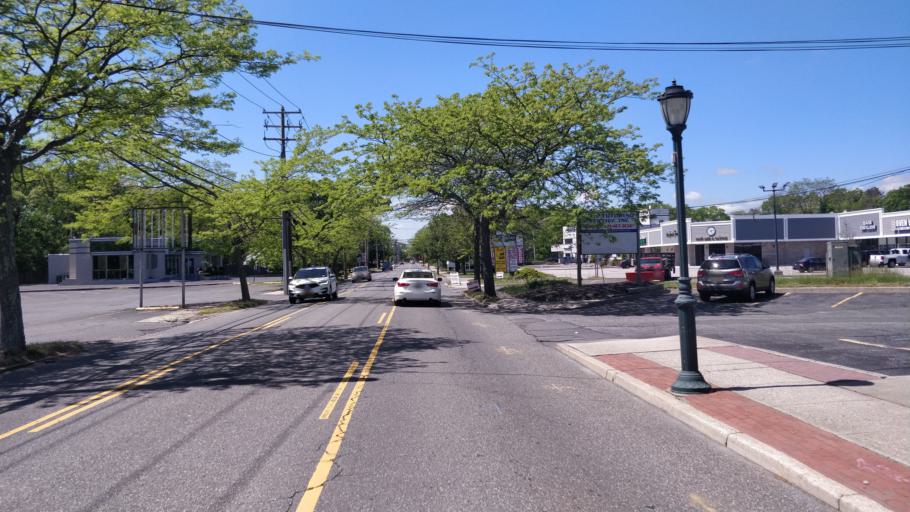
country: US
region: New York
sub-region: Suffolk County
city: Holbrook
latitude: 40.8071
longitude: -73.0739
